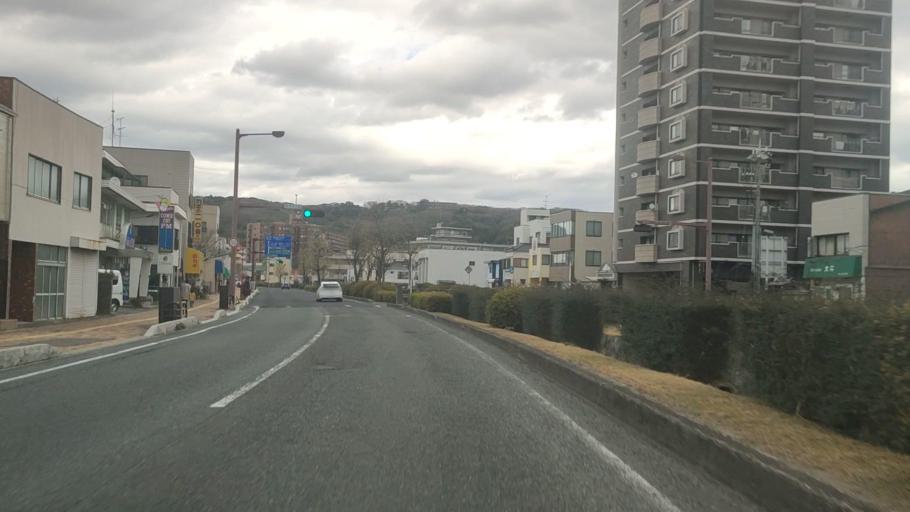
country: JP
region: Yamaguchi
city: Shimonoseki
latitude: 33.9639
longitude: 130.9422
